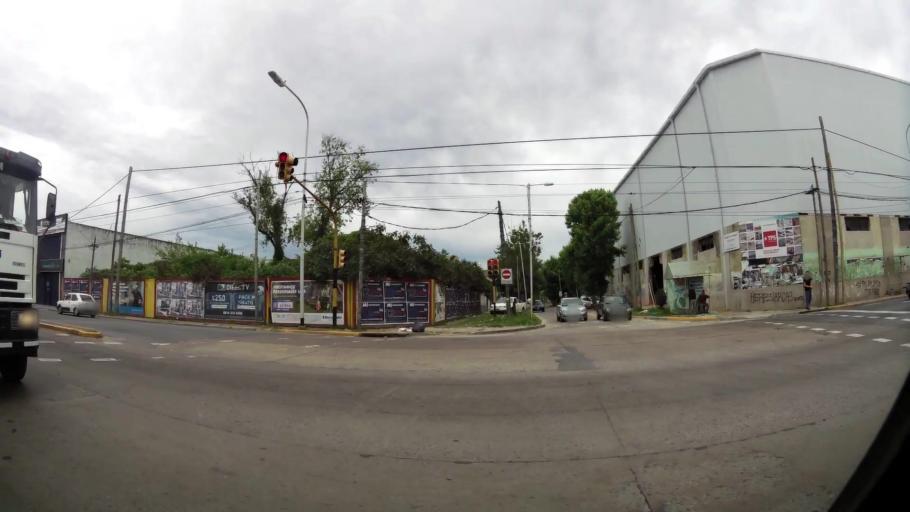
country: AR
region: Buenos Aires
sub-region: Partido de Avellaneda
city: Avellaneda
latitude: -34.6783
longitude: -58.3699
